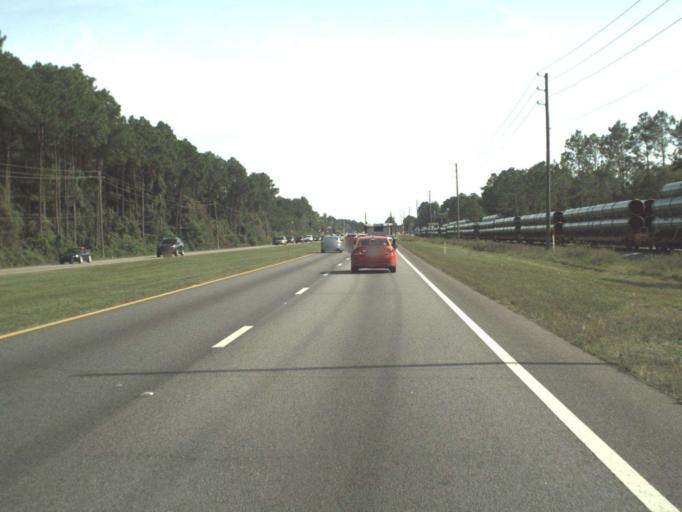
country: US
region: Florida
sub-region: Bay County
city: Hiland Park
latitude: 30.2094
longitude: -85.6126
